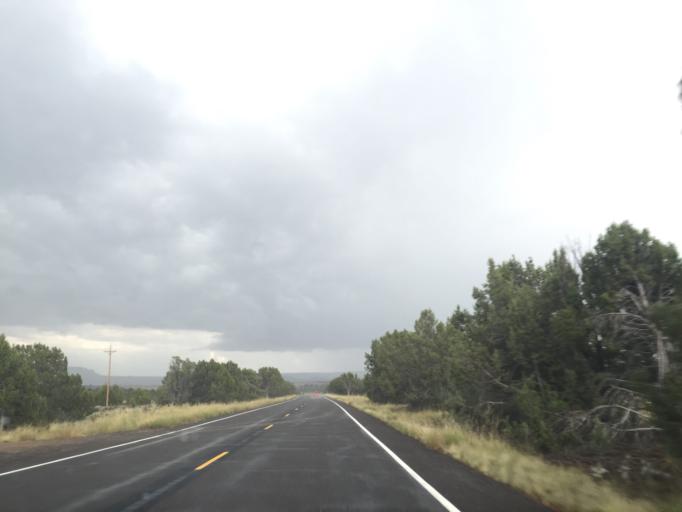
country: US
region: Utah
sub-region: Kane County
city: Kanab
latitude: 37.2482
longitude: -112.7582
